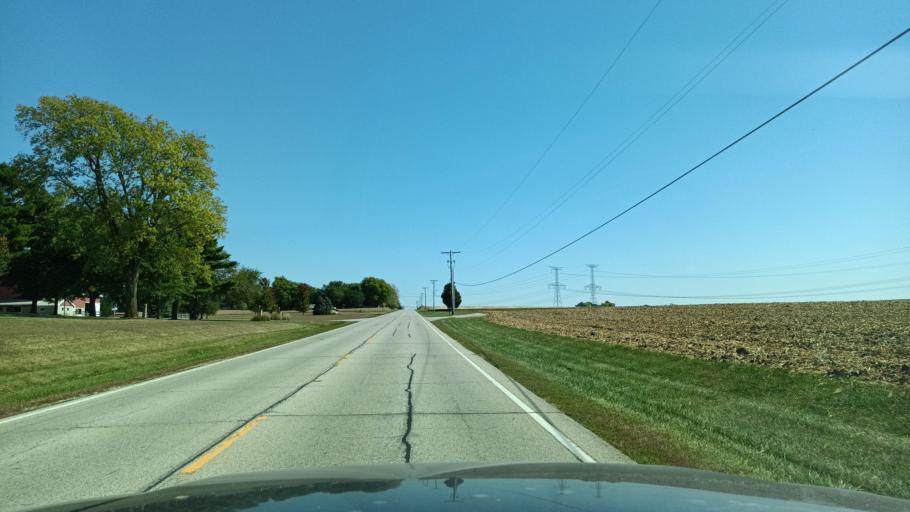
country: US
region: Illinois
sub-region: Tazewell County
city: Morton
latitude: 40.6137
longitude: -89.4160
